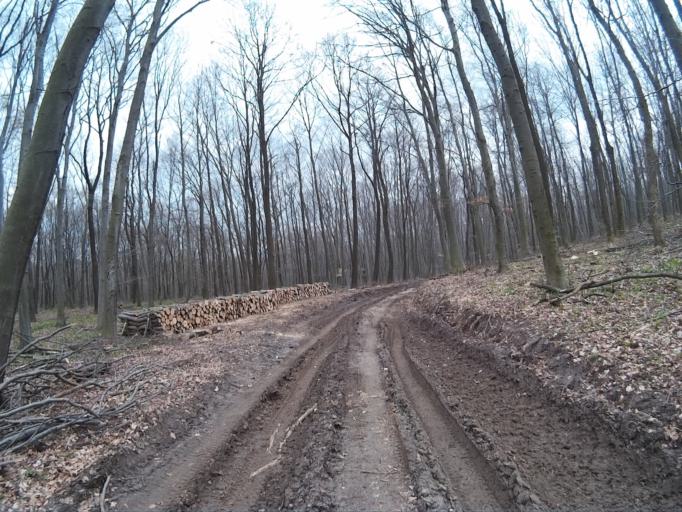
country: HU
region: Veszprem
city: Zirc
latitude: 47.1821
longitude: 17.8825
